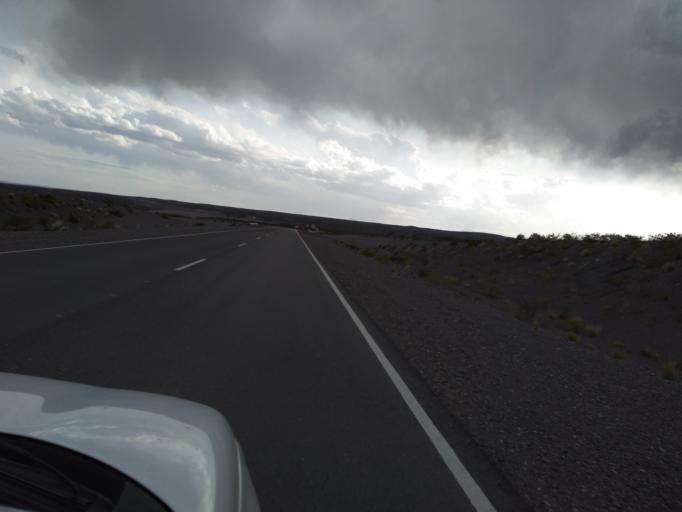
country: AR
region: Mendoza
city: La Consulta
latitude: -34.5427
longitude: -69.1624
